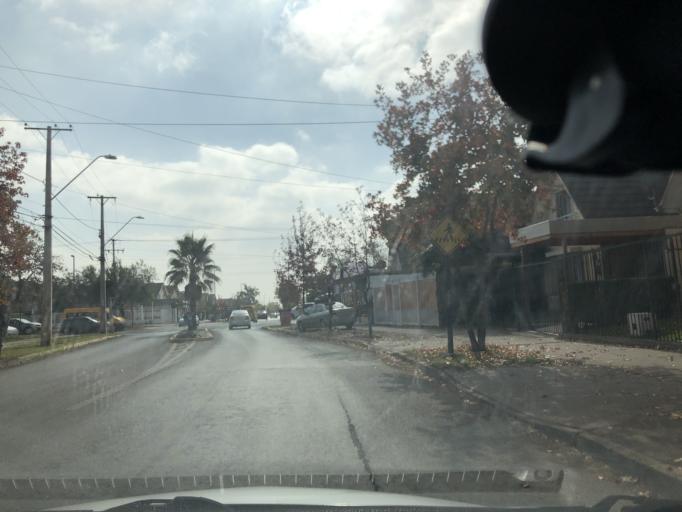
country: CL
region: Santiago Metropolitan
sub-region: Provincia de Cordillera
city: Puente Alto
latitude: -33.5998
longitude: -70.5839
